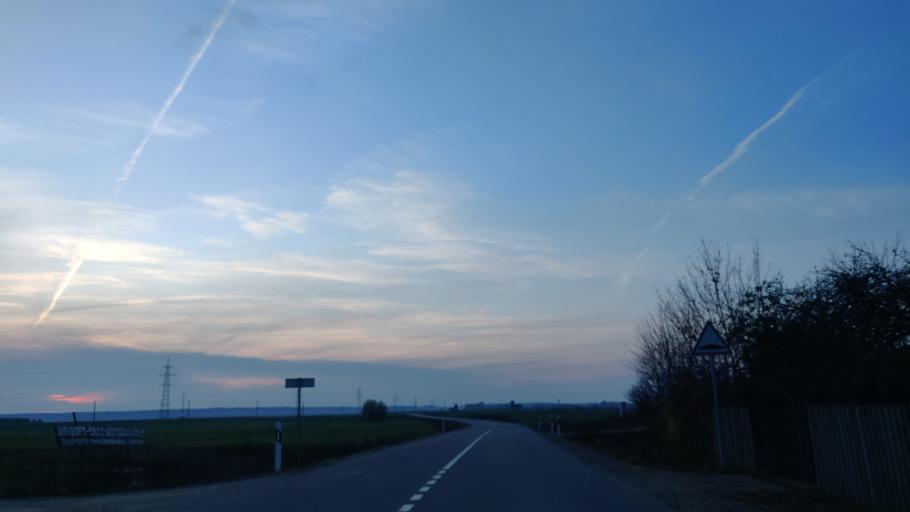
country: LT
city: Lentvaris
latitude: 54.6005
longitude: 25.0169
